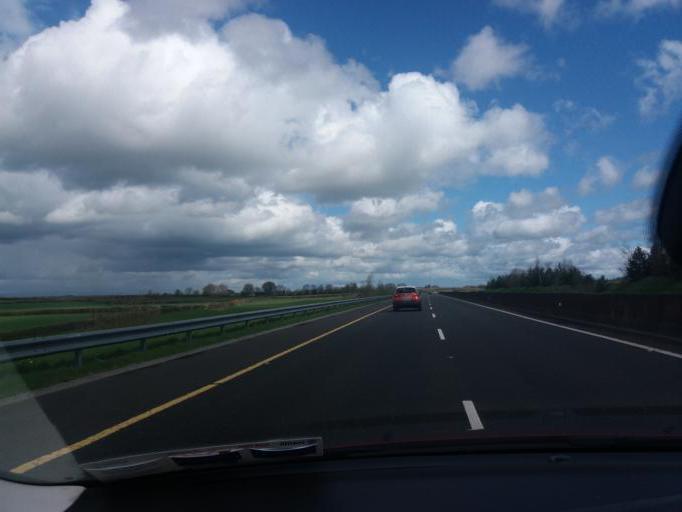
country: IE
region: Leinster
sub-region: Laois
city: Rathdowney
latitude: 52.7820
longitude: -7.5321
